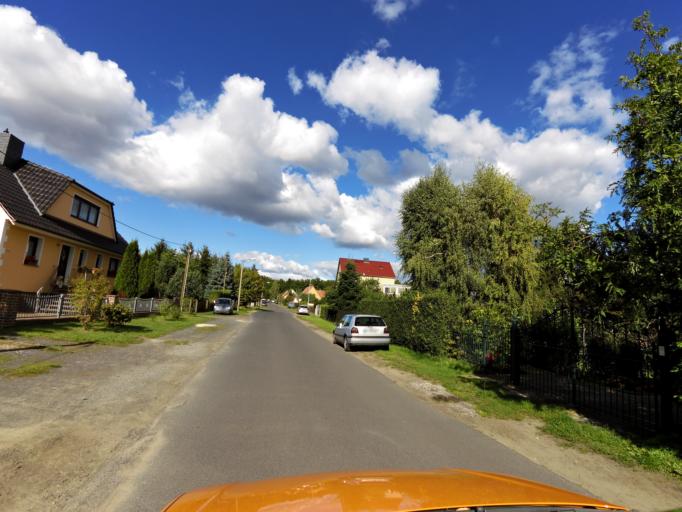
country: DE
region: Brandenburg
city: Luckenwalde
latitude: 52.0775
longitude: 13.1735
